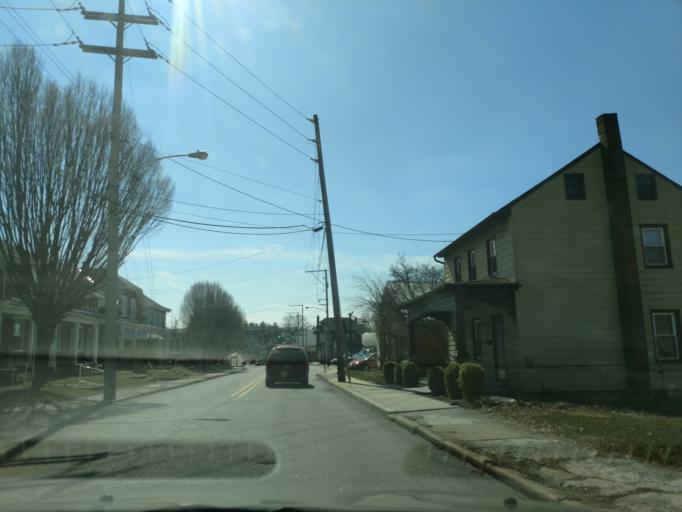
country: US
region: Pennsylvania
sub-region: Lebanon County
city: Lebanon
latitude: 40.3354
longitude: -76.4119
